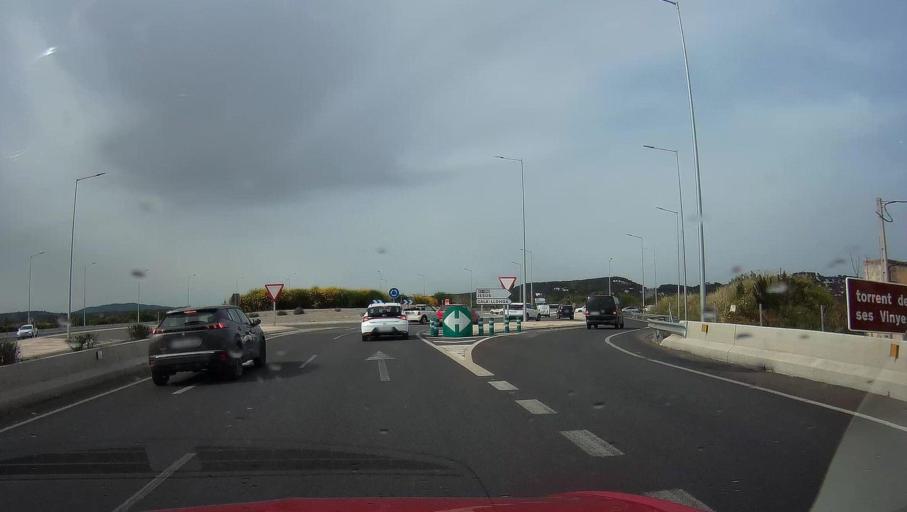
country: ES
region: Balearic Islands
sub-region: Illes Balears
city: Ibiza
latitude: 38.9347
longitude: 1.4444
